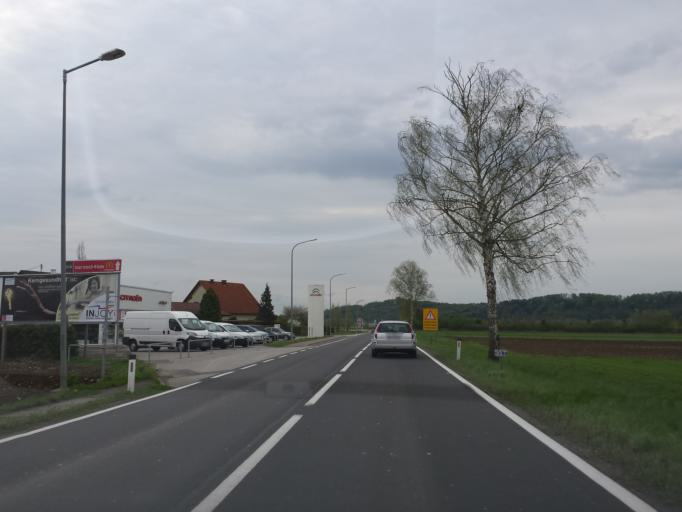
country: AT
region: Styria
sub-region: Politischer Bezirk Hartberg-Fuerstenfeld
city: Soechau
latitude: 47.0750
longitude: 16.0001
